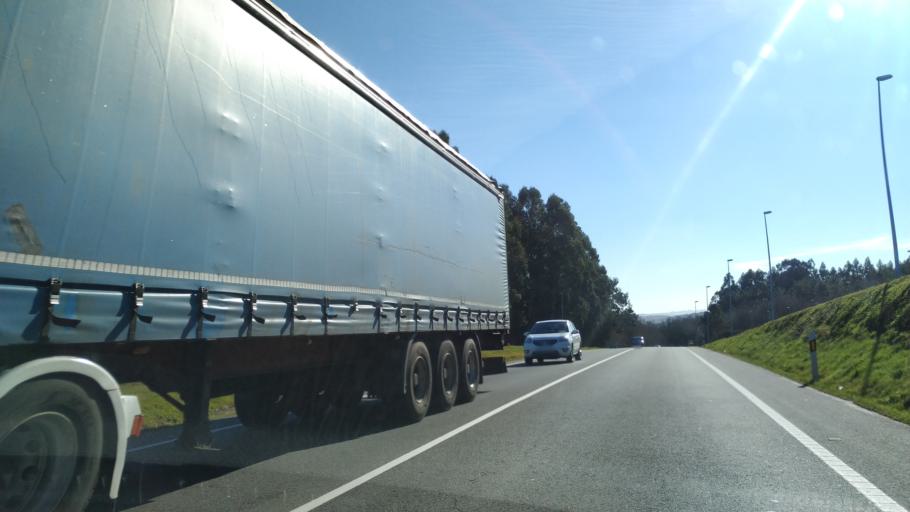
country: ES
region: Galicia
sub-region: Provincia de Pontevedra
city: Silleda
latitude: 42.6924
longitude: -8.2248
